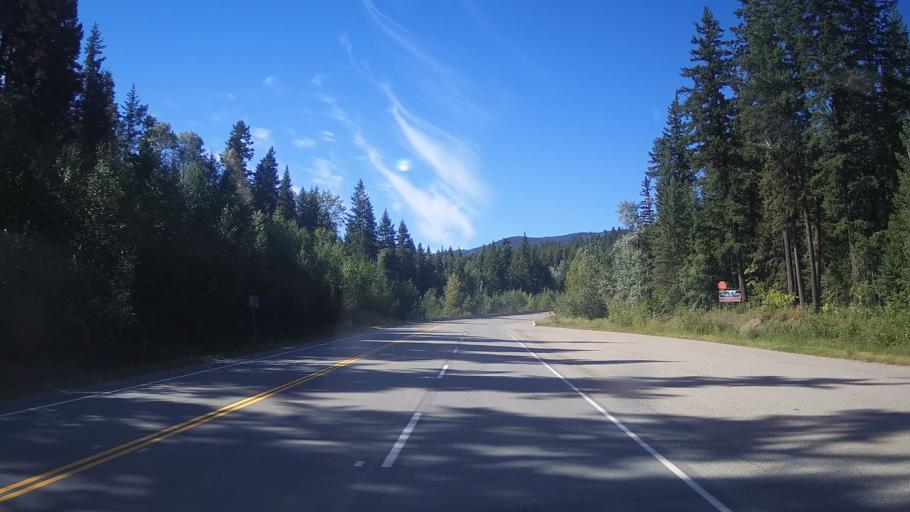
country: CA
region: British Columbia
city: Kamloops
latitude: 51.4646
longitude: -120.2405
